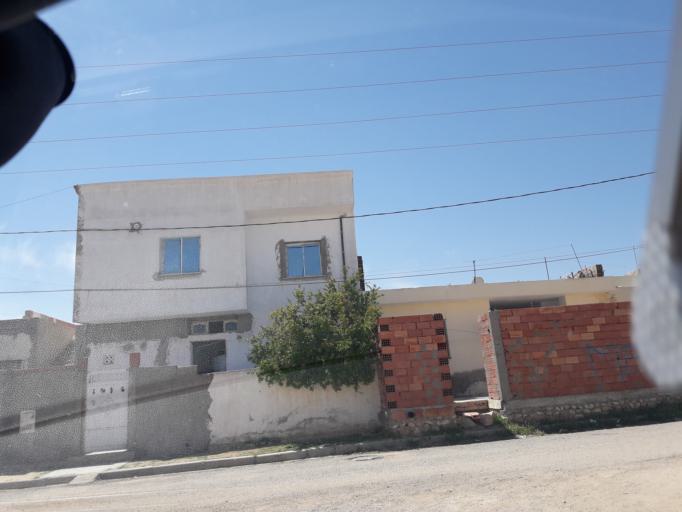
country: TN
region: Safaqis
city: Sfax
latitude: 34.7386
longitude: 10.5233
